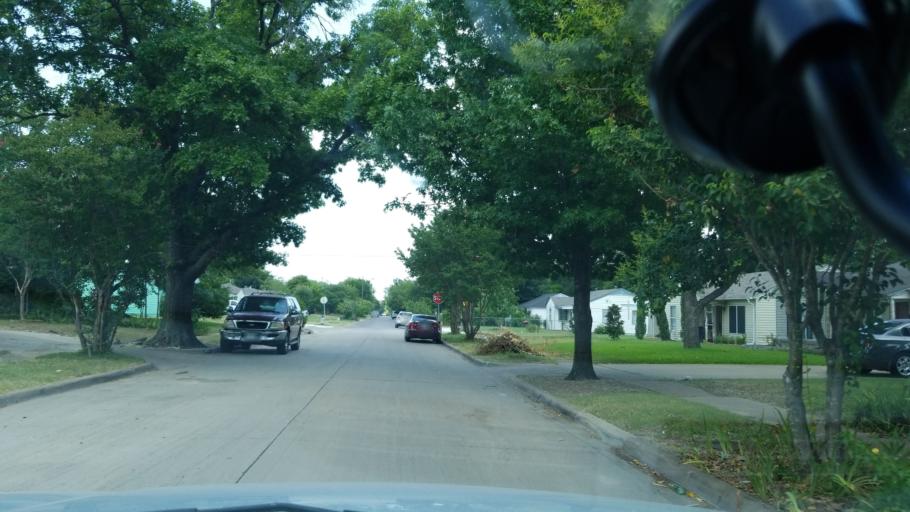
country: US
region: Texas
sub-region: Dallas County
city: Cockrell Hill
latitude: 32.7245
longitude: -96.8726
